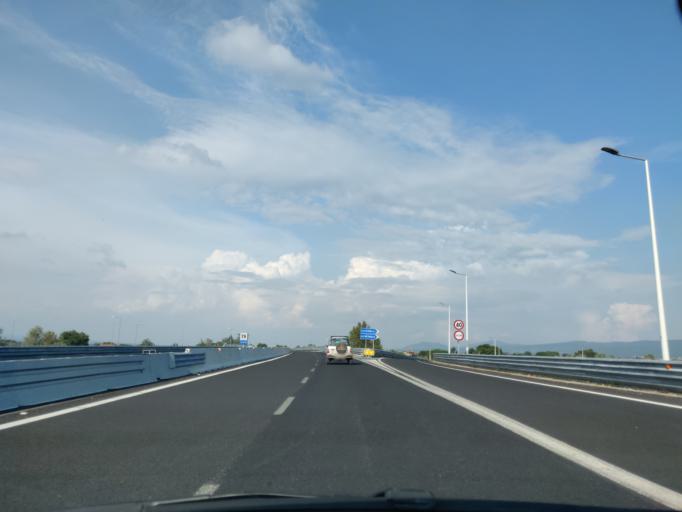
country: IT
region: Latium
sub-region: Provincia di Viterbo
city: Blera
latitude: 42.3057
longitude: 11.9885
